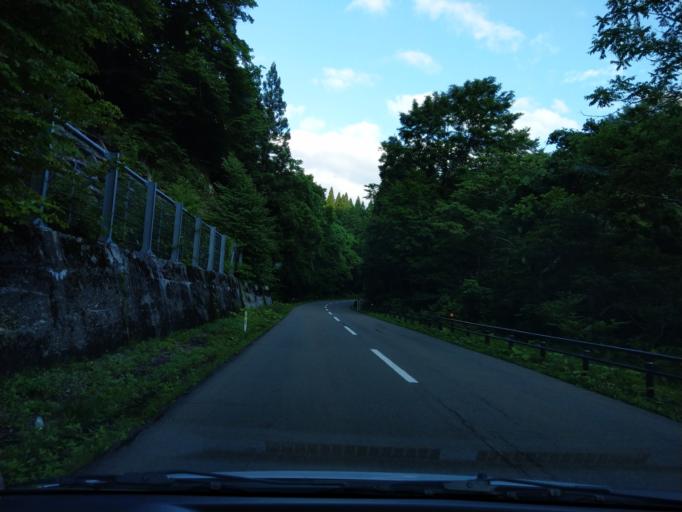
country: JP
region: Akita
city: Kakunodatemachi
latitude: 39.8792
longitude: 140.4749
